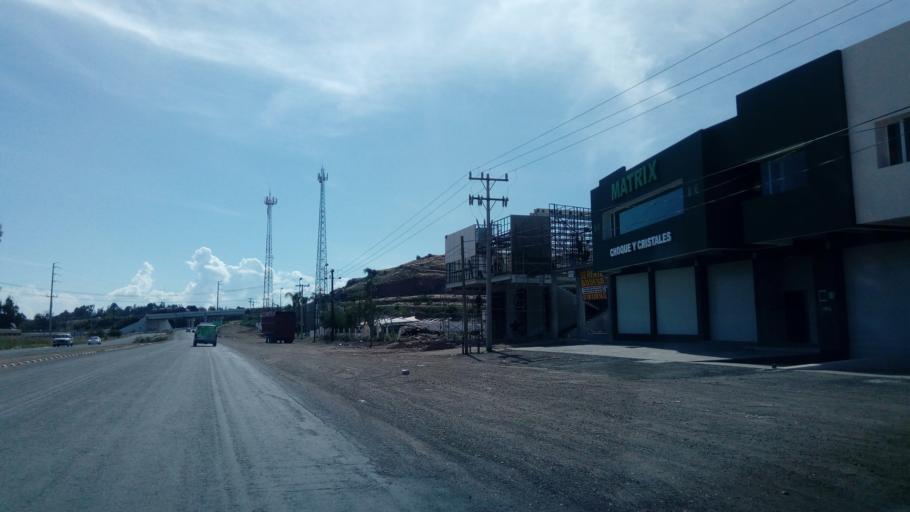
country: MX
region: Durango
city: Victoria de Durango
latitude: 24.0716
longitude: -104.6573
